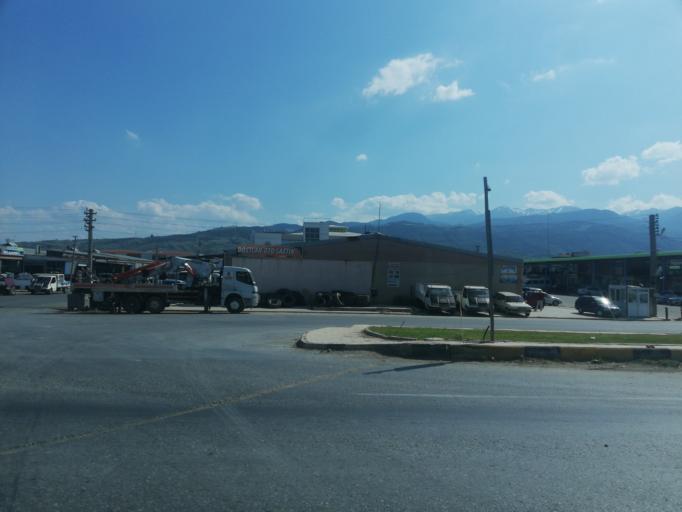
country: TR
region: Manisa
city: Alasehir
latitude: 38.3585
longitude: 28.5429
